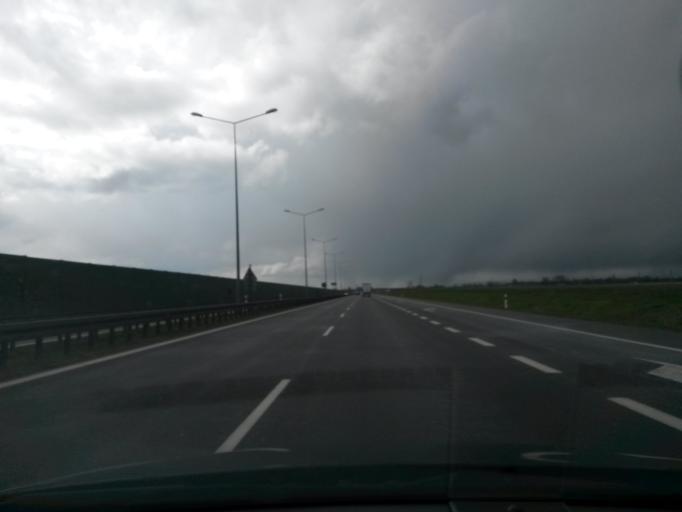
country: PL
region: Greater Poland Voivodeship
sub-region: Powiat poznanski
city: Kleszczewo
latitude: 52.3135
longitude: 17.1420
